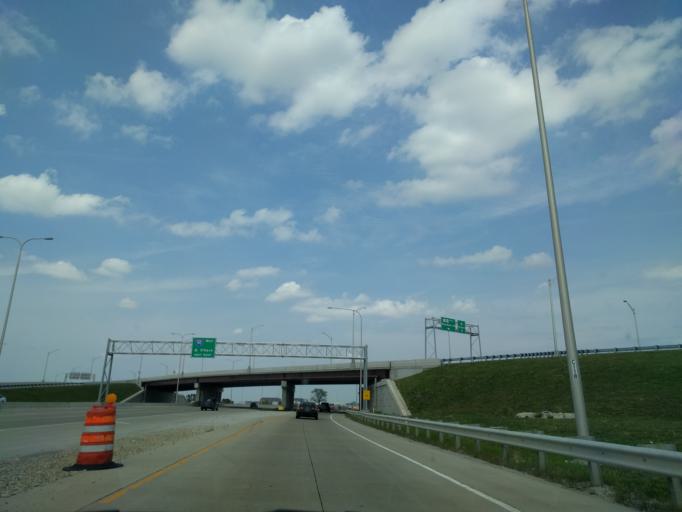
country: US
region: Illinois
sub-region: Cook County
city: Rosemont
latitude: 41.9760
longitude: -87.8784
